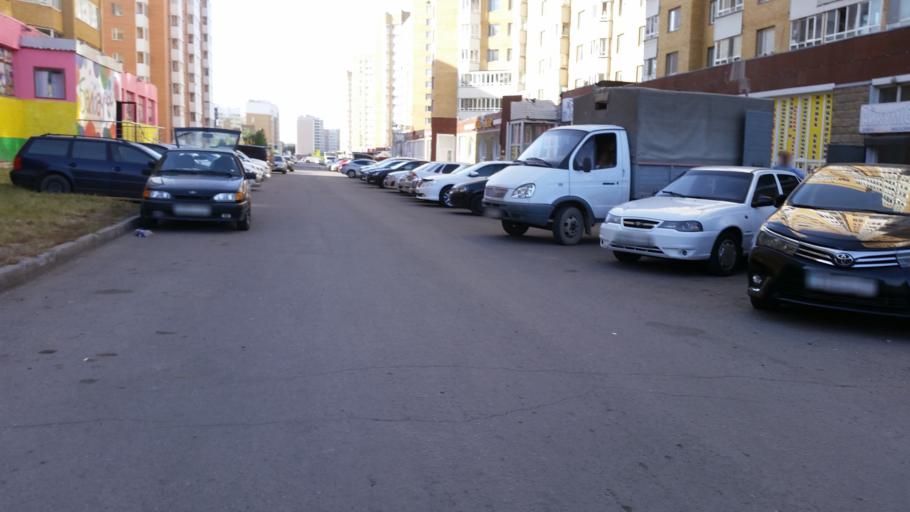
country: KZ
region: Astana Qalasy
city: Astana
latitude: 51.1563
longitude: 71.5093
